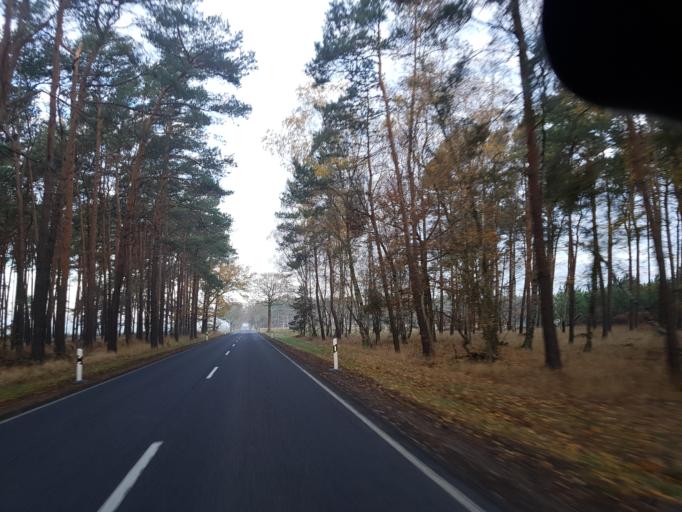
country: DE
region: Saxony-Anhalt
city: Seyda
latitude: 51.8980
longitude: 12.8507
